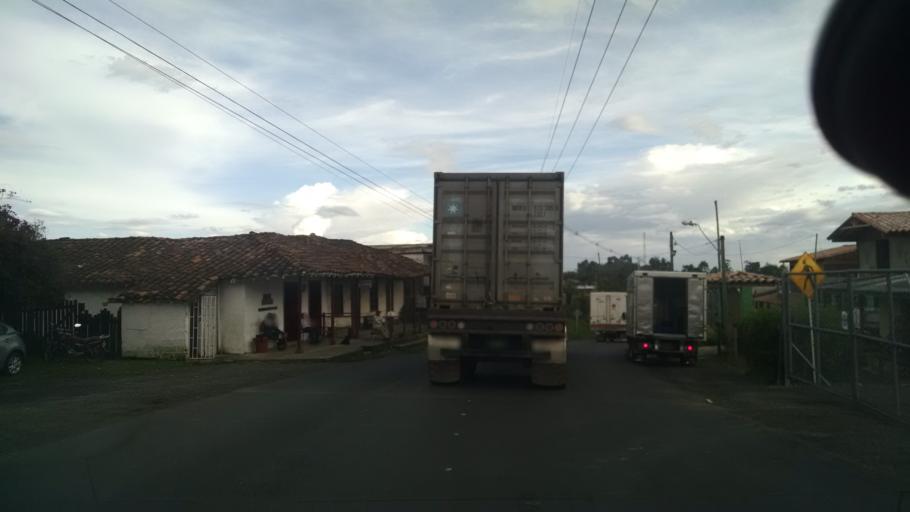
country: CO
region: Antioquia
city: Santa Barbara
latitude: 5.9254
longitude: -75.5776
